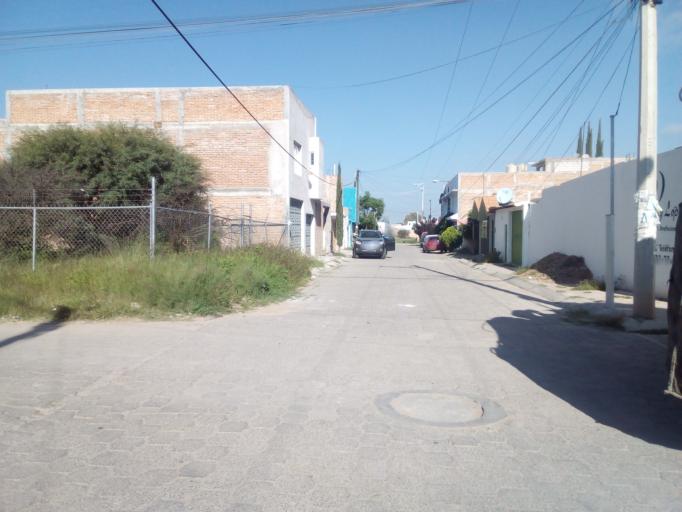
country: MX
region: Guanajuato
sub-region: San Luis de la Paz
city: San Ignacio
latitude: 21.2962
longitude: -100.5335
